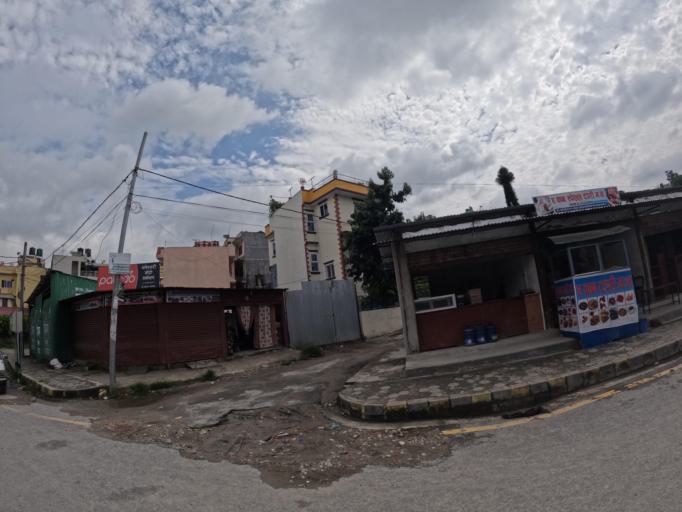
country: NP
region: Central Region
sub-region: Bagmati Zone
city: Kathmandu
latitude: 27.7517
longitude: 85.3166
